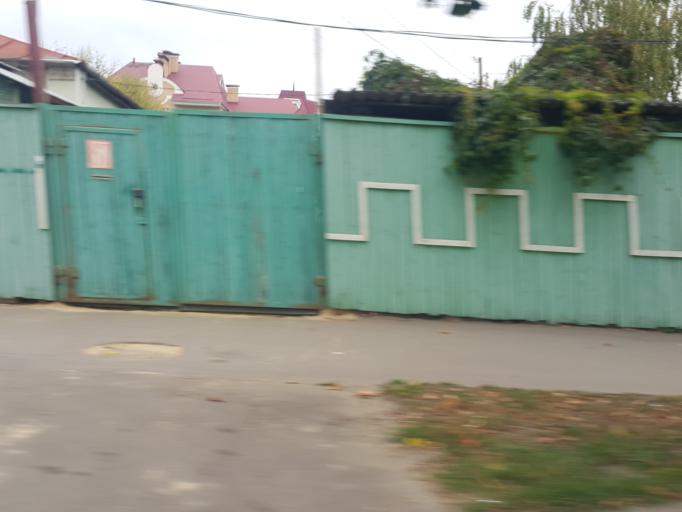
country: RU
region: Tambov
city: Tambov
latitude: 52.7128
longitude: 41.4569
